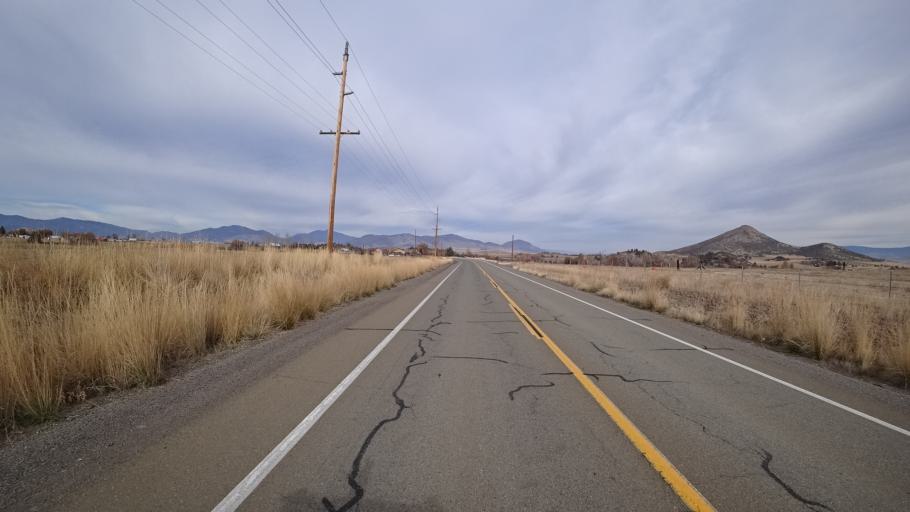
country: US
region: California
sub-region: Siskiyou County
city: Montague
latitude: 41.6958
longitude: -122.5351
